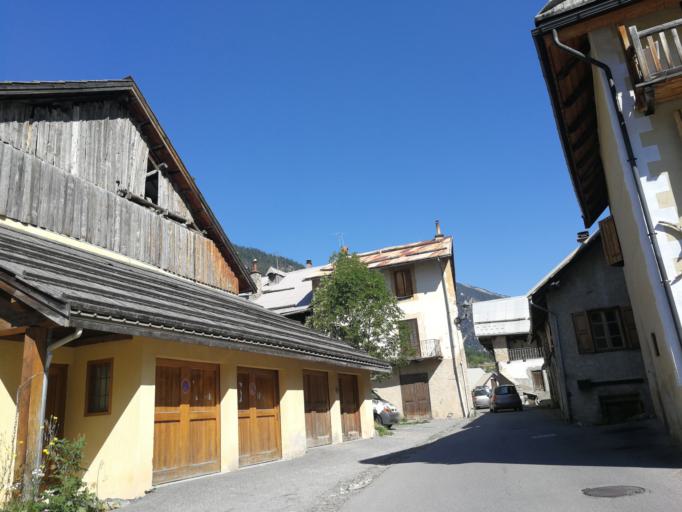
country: FR
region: Provence-Alpes-Cote d'Azur
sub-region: Departement des Hautes-Alpes
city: Briancon
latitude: 44.9496
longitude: 6.6782
